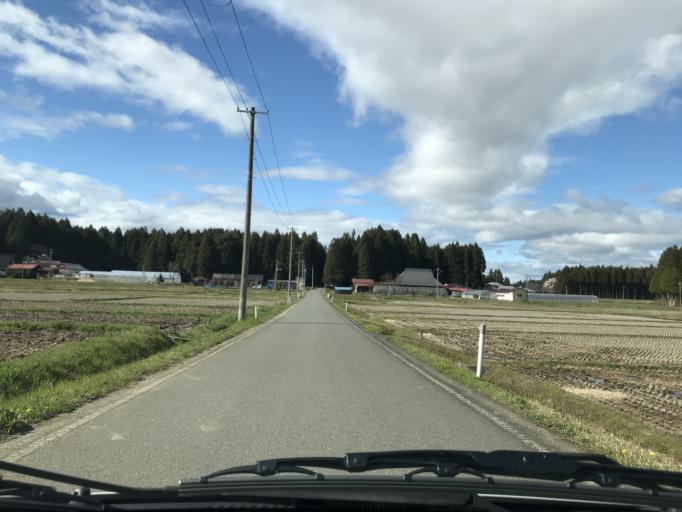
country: JP
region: Iwate
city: Mizusawa
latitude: 39.1079
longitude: 141.0925
